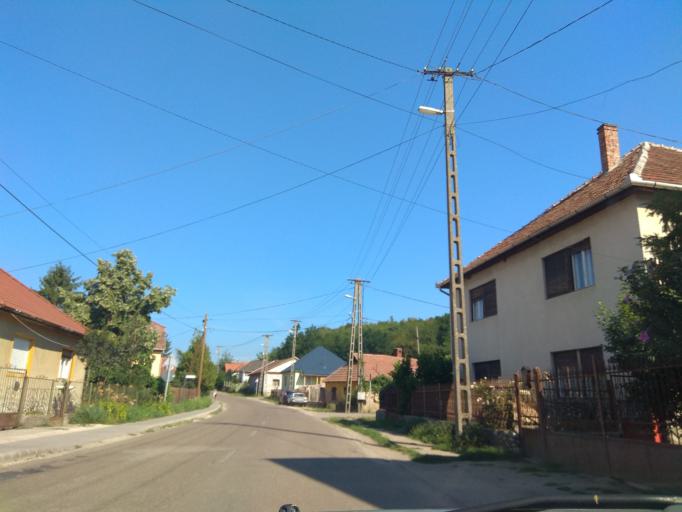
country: HU
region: Borsod-Abauj-Zemplen
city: Harsany
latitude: 47.9857
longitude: 20.7804
